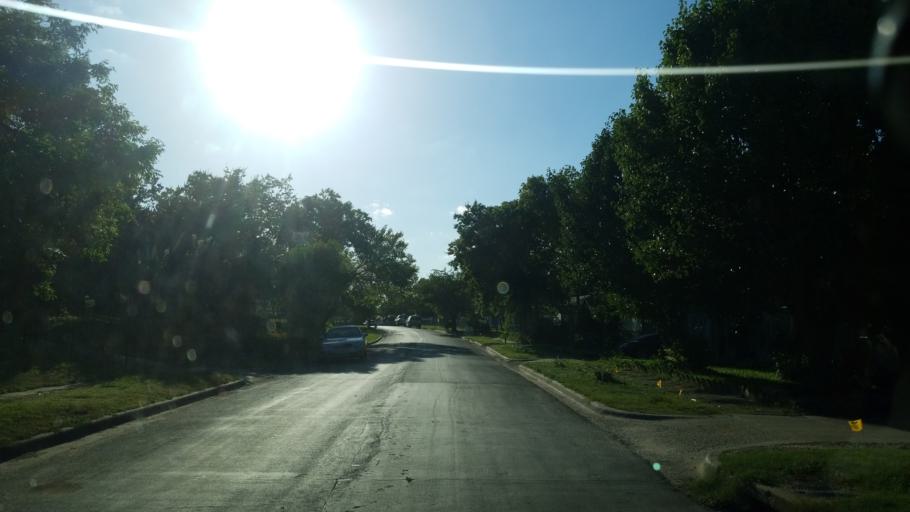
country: US
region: Texas
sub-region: Dallas County
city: Dallas
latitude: 32.7781
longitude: -96.7099
